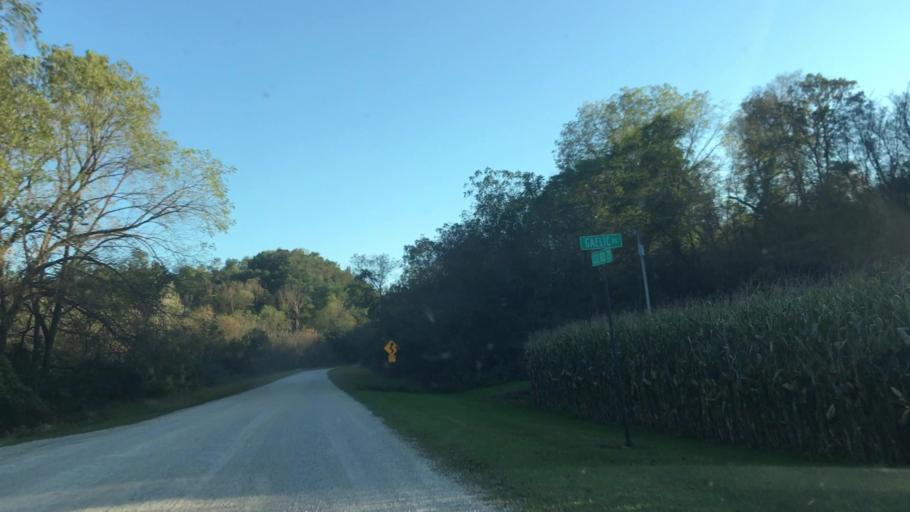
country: US
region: Minnesota
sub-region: Fillmore County
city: Preston
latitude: 43.7570
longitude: -92.0299
